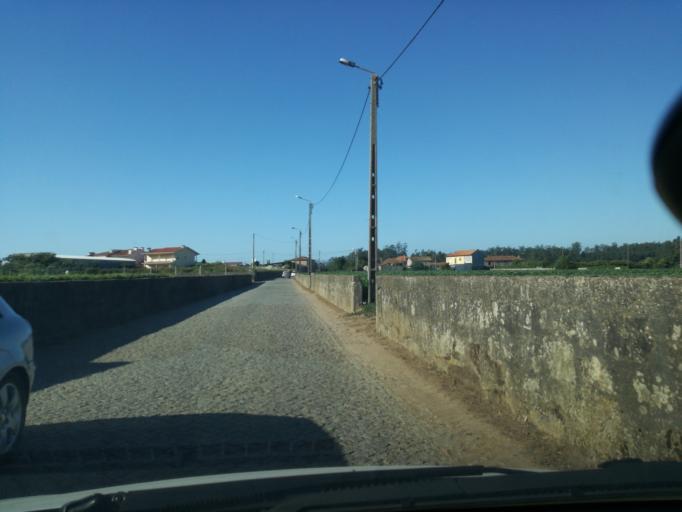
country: PT
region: Porto
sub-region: Matosinhos
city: Lavra
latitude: 41.2874
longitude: -8.6928
